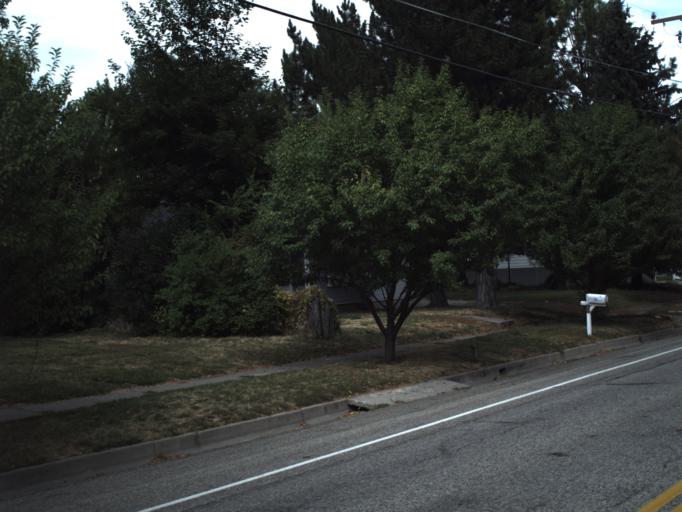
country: US
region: Utah
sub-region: Cache County
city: Wellsville
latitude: 41.6432
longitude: -111.9342
